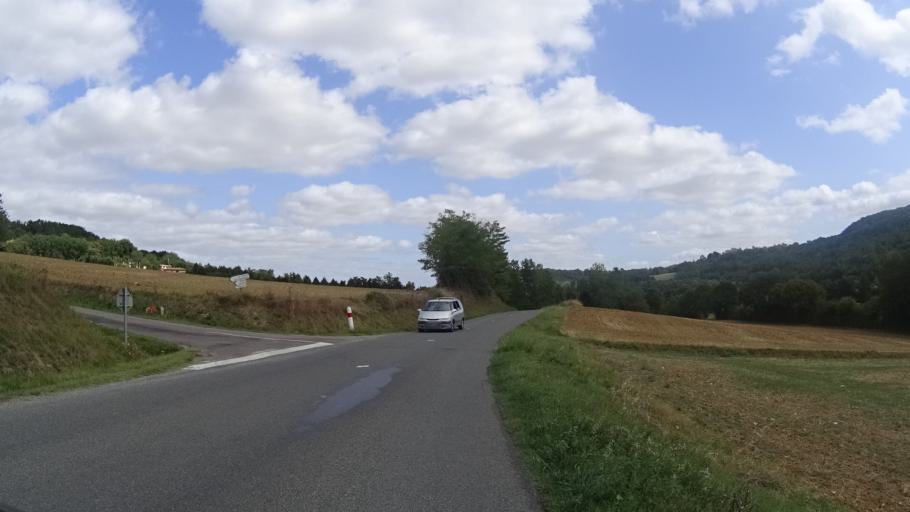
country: FR
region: Aquitaine
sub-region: Departement du Lot-et-Garonne
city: Pont-du-Casse
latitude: 44.2501
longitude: 0.6840
